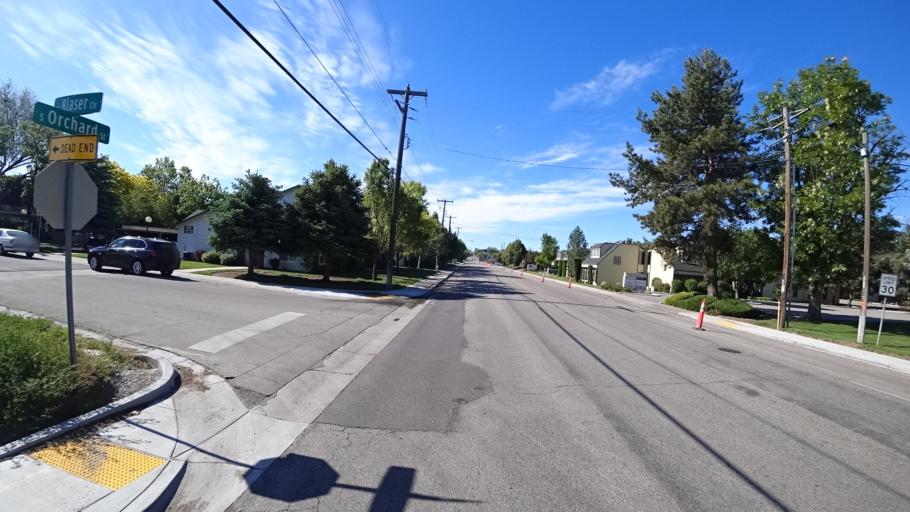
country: US
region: Idaho
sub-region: Ada County
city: Garden City
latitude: 43.5964
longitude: -116.2436
